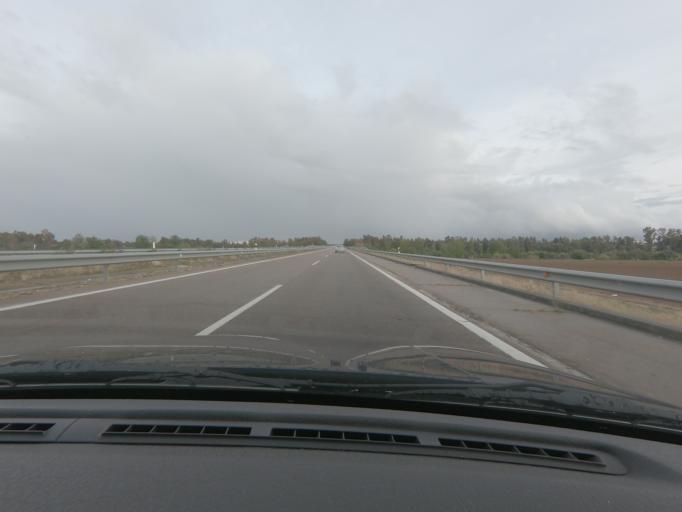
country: ES
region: Extremadura
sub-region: Provincia de Badajoz
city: Badajoz
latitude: 38.9025
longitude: -6.9311
